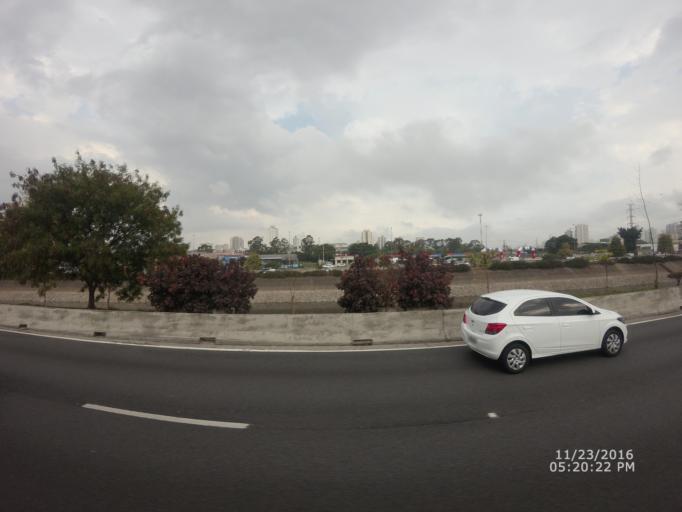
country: BR
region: Sao Paulo
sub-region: Guarulhos
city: Guarulhos
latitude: -23.5215
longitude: -46.5571
